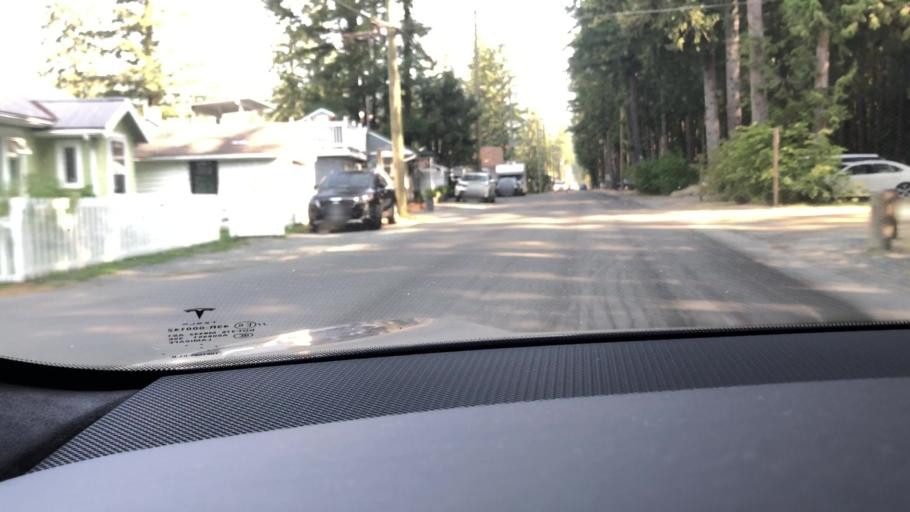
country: CA
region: British Columbia
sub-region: Fraser Valley Regional District
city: Chilliwack
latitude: 49.0688
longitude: -121.9761
